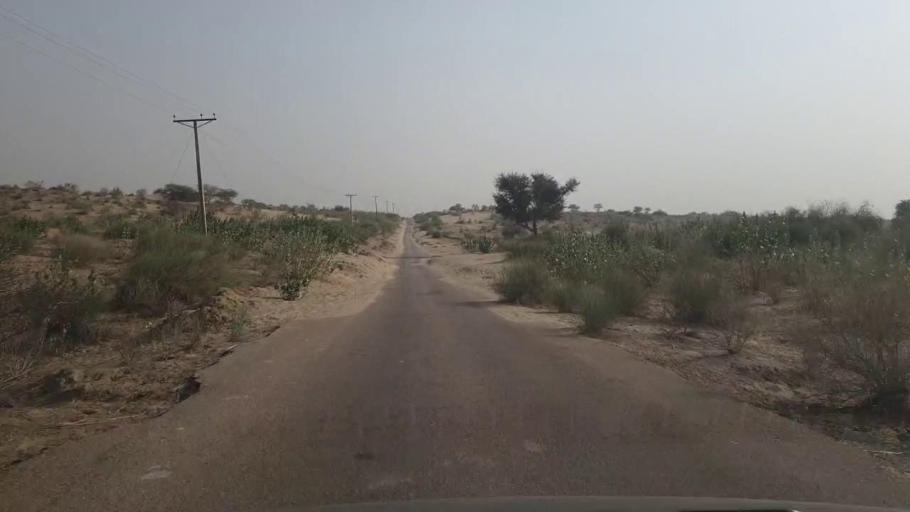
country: PK
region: Sindh
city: Chor
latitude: 25.5542
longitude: 69.9582
